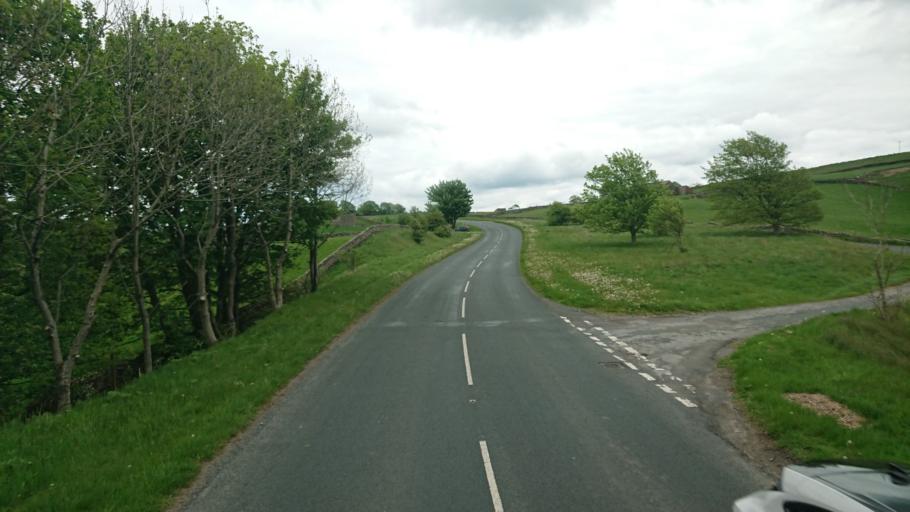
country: GB
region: England
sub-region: County Durham
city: Bowes
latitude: 54.3077
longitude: -2.1157
